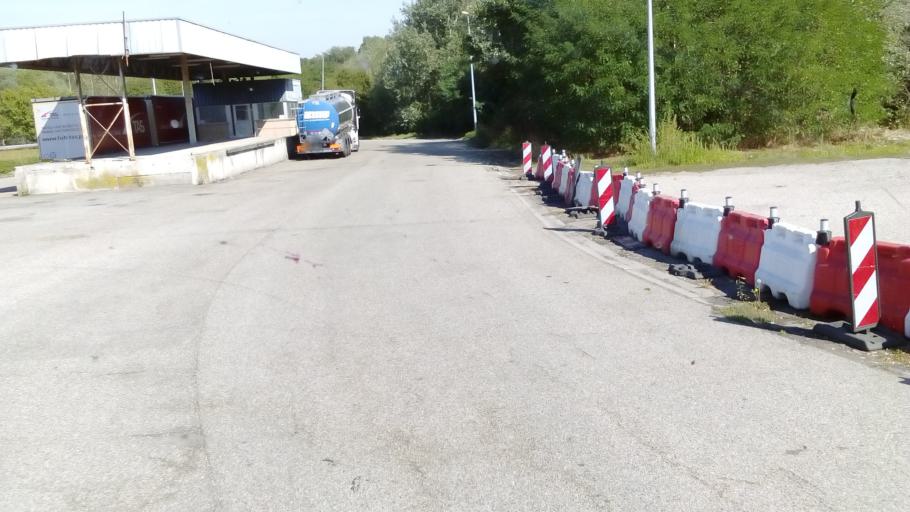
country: DE
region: Rheinland-Pfalz
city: Scheibenhardt
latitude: 48.9763
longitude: 8.1573
